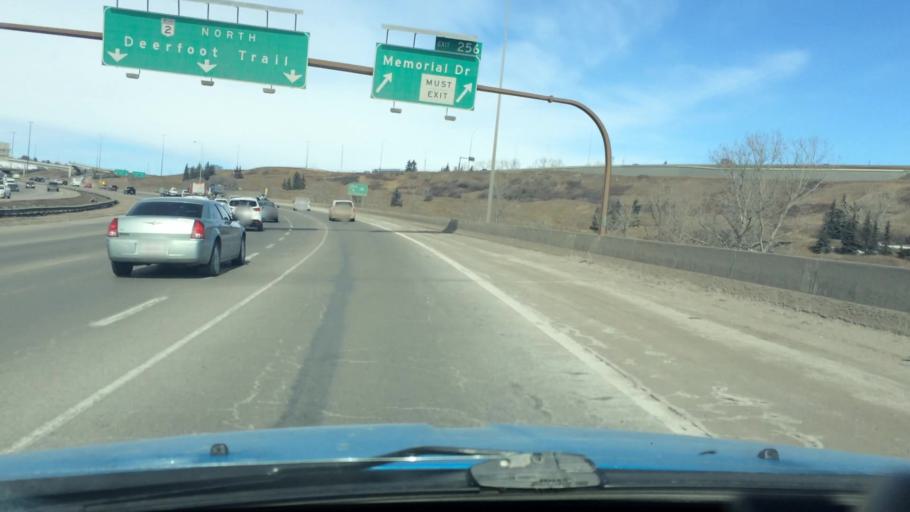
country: CA
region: Alberta
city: Calgary
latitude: 51.0427
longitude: -114.0079
